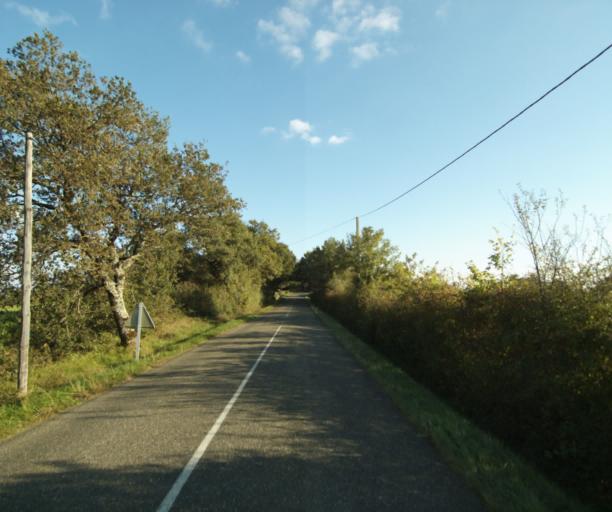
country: FR
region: Midi-Pyrenees
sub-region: Departement du Gers
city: Eauze
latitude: 43.7623
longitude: 0.1293
